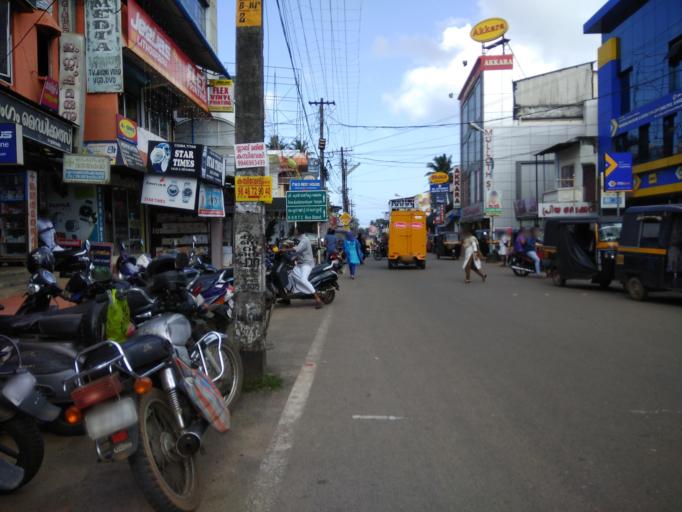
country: IN
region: Kerala
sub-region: Thrissur District
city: Irinjalakuda
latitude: 10.3468
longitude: 76.2068
